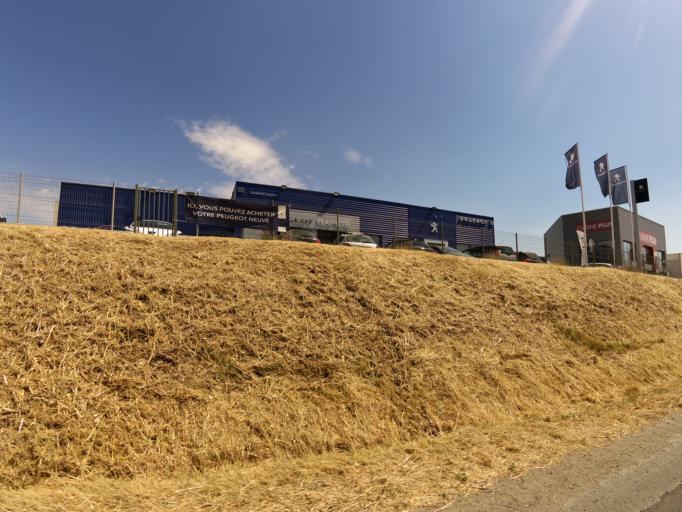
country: FR
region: Languedoc-Roussillon
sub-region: Departement de l'Herault
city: Vendargues
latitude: 43.6527
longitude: 3.9729
